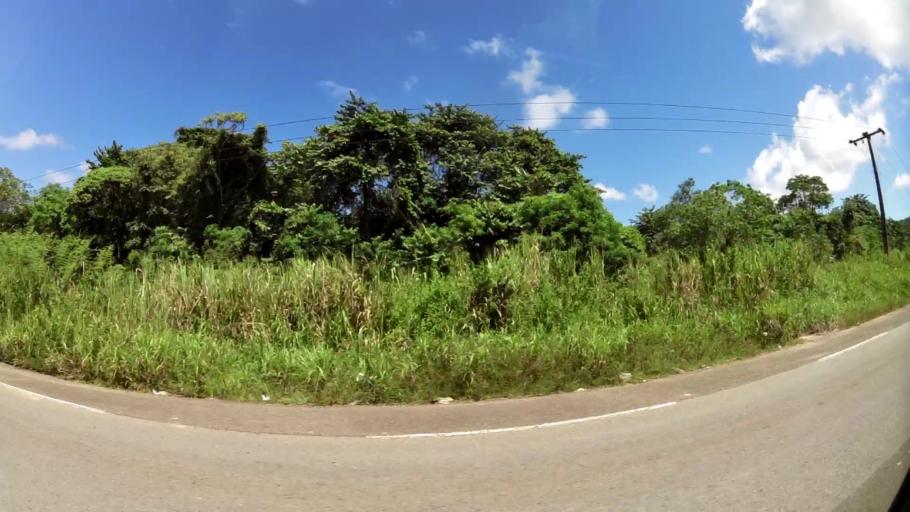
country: GF
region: Guyane
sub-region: Guyane
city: Matoury
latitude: 4.8635
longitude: -52.3333
